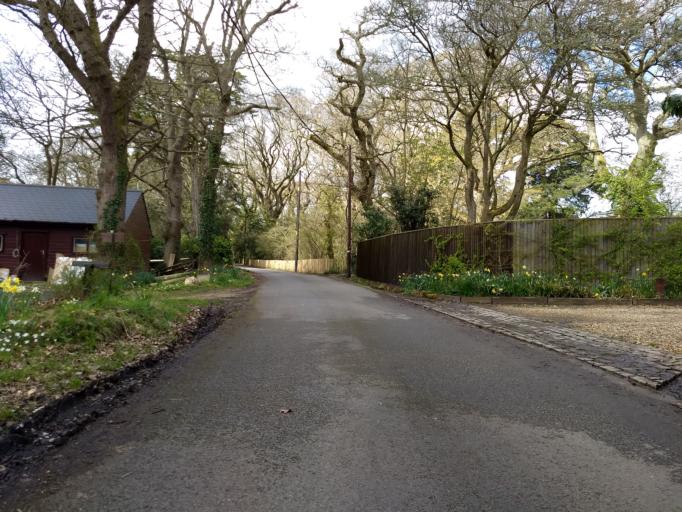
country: GB
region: England
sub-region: Isle of Wight
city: Ryde
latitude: 50.7370
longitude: -1.2170
